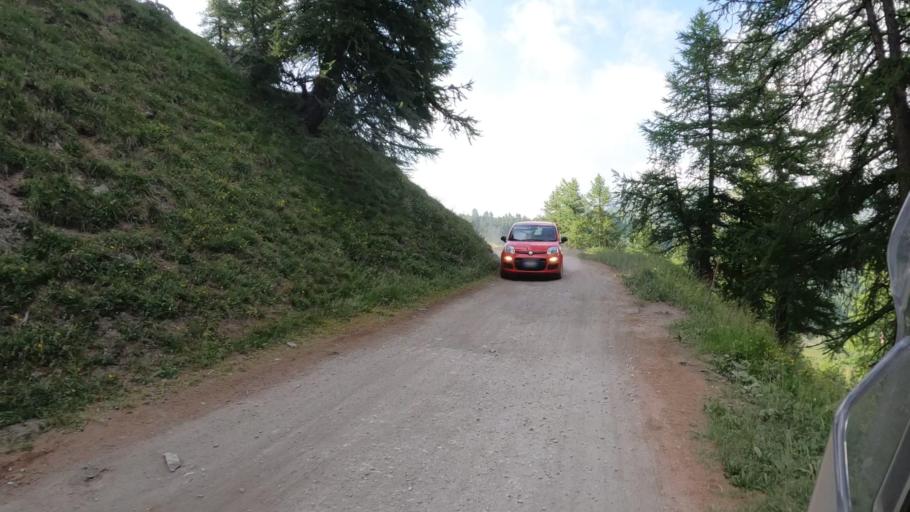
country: IT
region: Piedmont
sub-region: Provincia di Torino
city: Sauze d'Oulx
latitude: 45.0110
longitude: 6.8919
